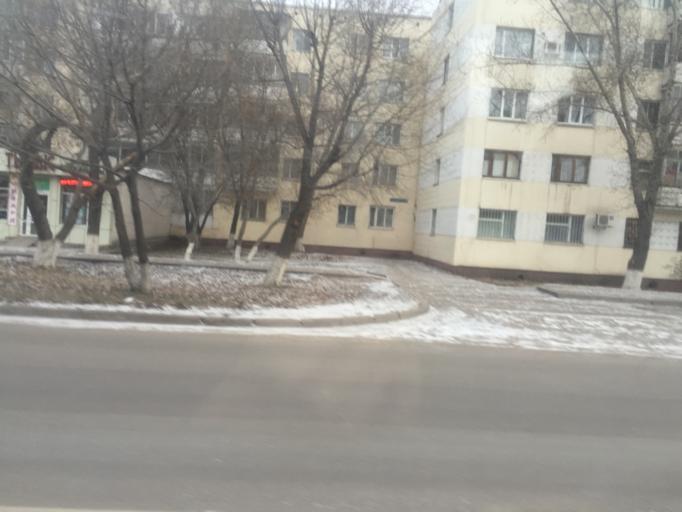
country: KZ
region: Astana Qalasy
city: Astana
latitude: 51.1963
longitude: 71.3929
